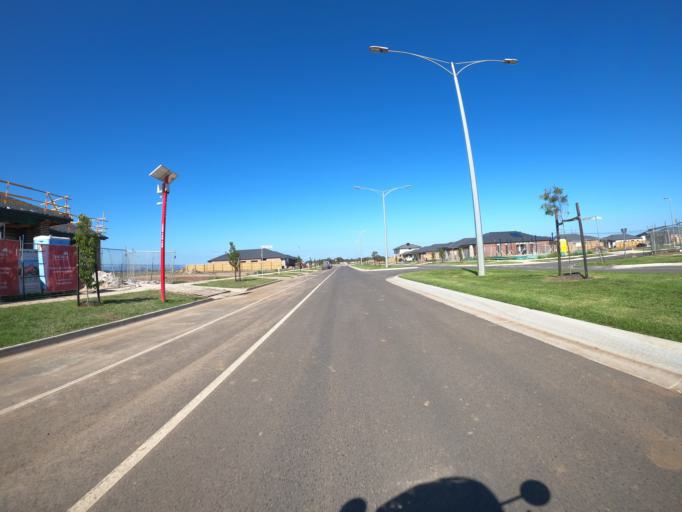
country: AU
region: Victoria
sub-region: Hume
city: Craigieburn
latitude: -37.5444
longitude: 144.8905
